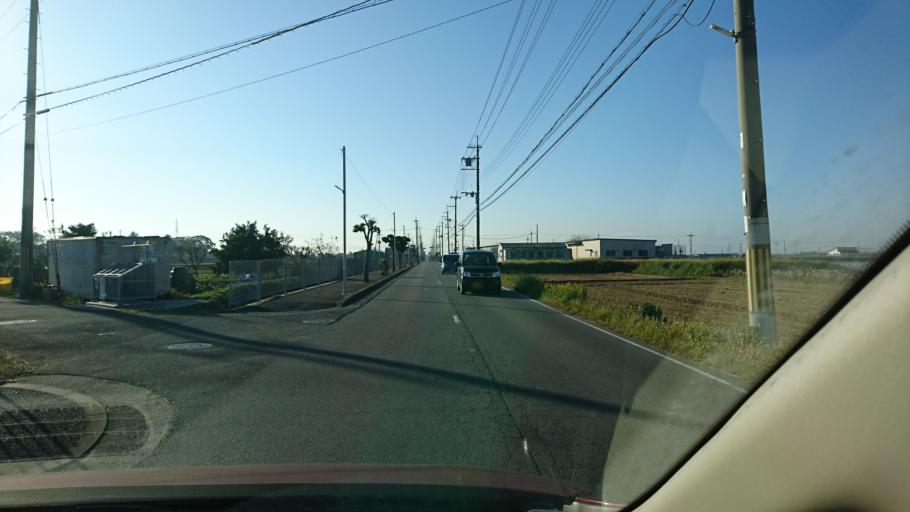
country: JP
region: Hyogo
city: Miki
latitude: 34.7463
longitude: 134.9212
